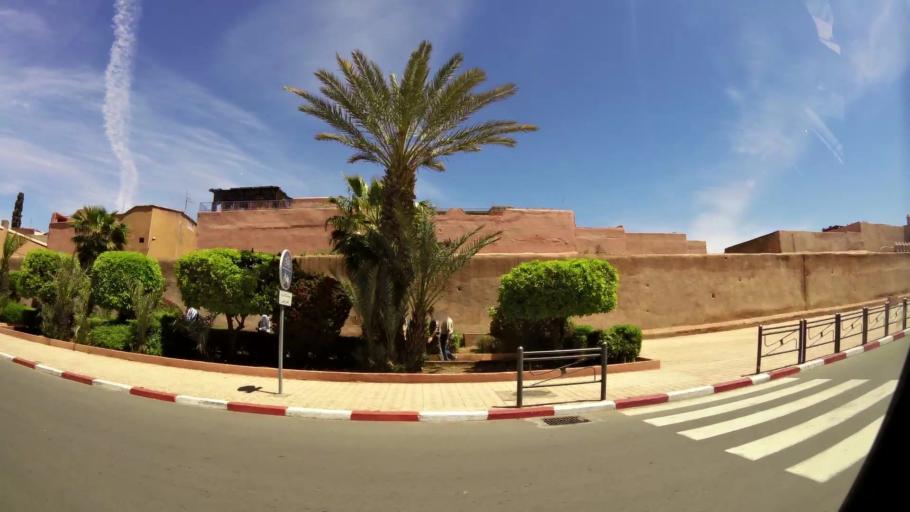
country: MA
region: Marrakech-Tensift-Al Haouz
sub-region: Marrakech
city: Marrakesh
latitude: 31.6112
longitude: -7.9894
